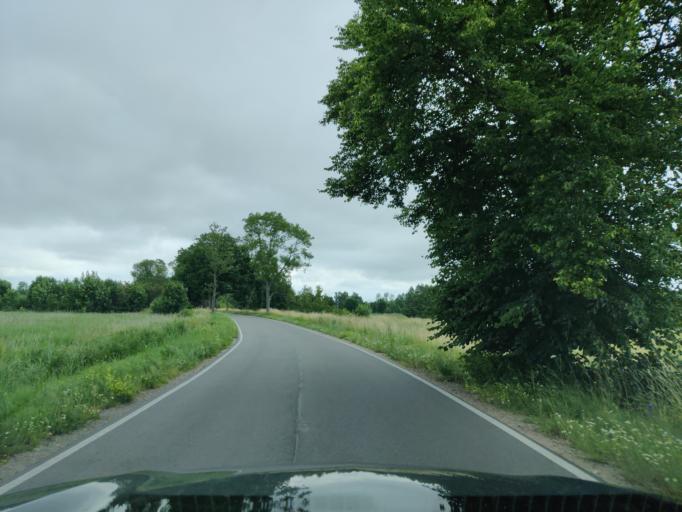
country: PL
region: Warmian-Masurian Voivodeship
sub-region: Powiat gizycki
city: Ryn
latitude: 53.8779
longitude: 21.5844
